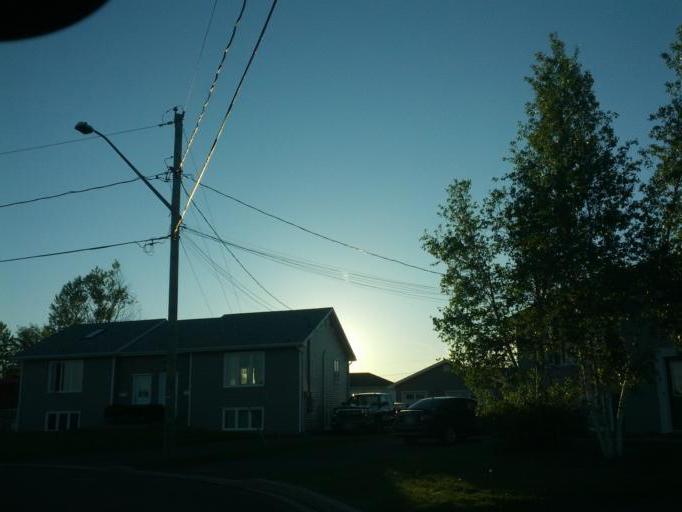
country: CA
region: New Brunswick
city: Moncton
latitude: 46.1200
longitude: -64.8505
